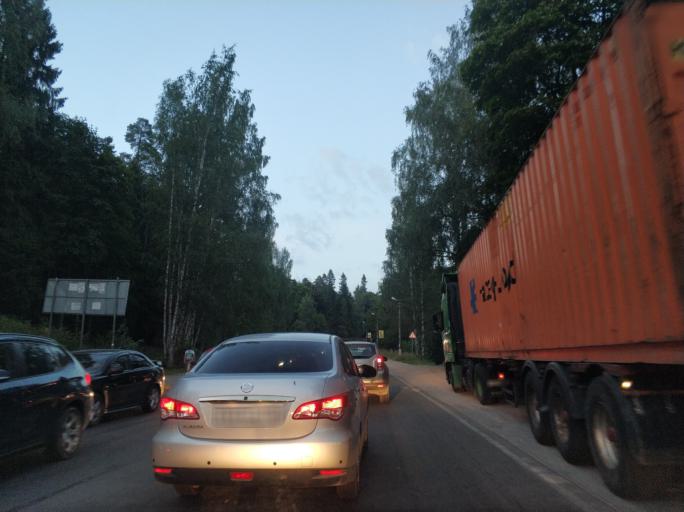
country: RU
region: Leningrad
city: Vsevolozhsk
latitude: 60.0345
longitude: 30.6373
